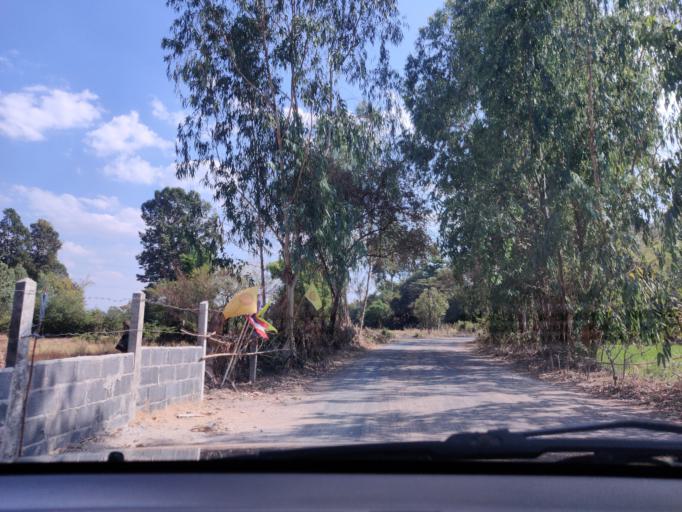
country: TH
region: Sisaket
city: Si Sa Ket
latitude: 15.0768
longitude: 104.3505
